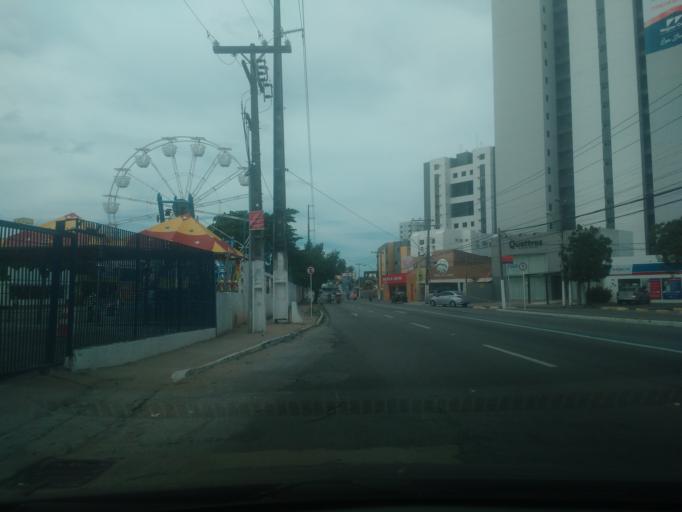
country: BR
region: Alagoas
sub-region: Maceio
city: Maceio
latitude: -9.6480
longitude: -35.7133
